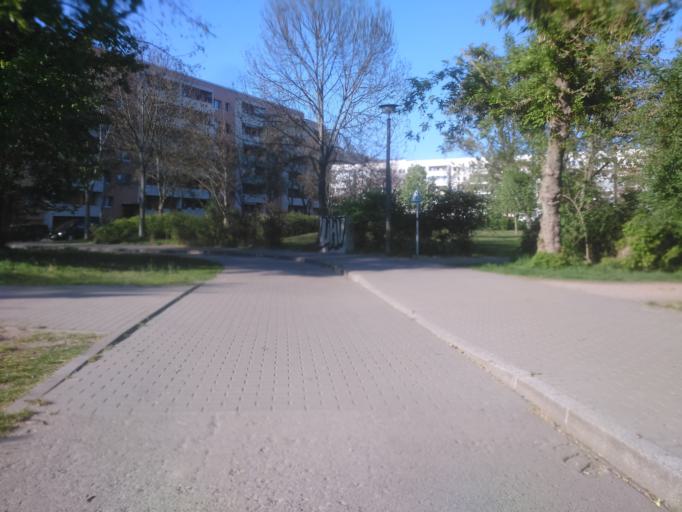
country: DE
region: Berlin
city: Neu-Hohenschoenhausen
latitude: 52.5609
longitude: 13.5055
